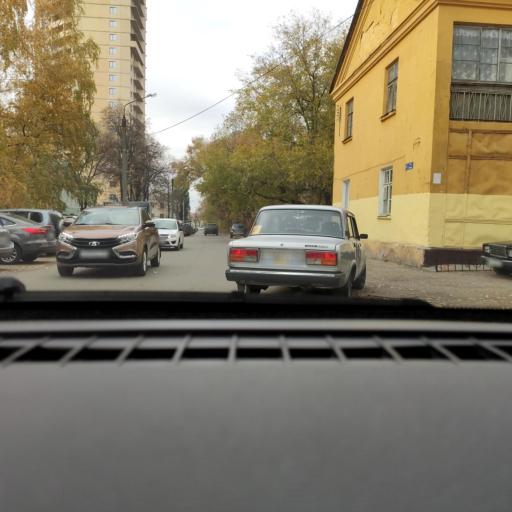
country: RU
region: Voronezj
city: Voronezh
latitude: 51.6972
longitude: 39.1861
